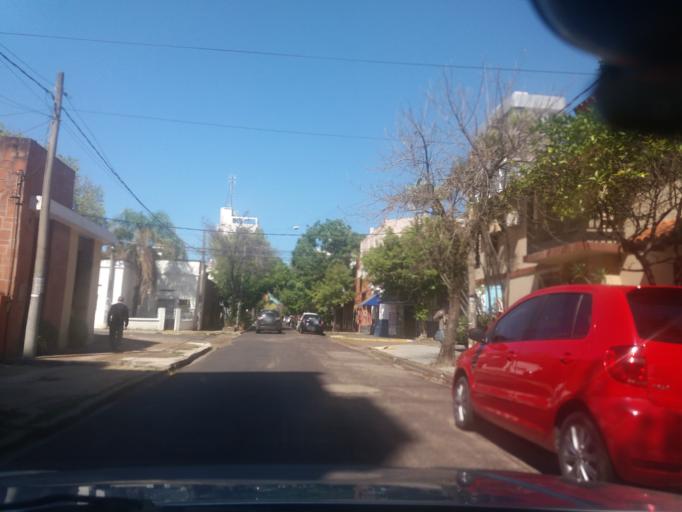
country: AR
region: Corrientes
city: Corrientes
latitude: -27.4697
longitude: -58.8470
